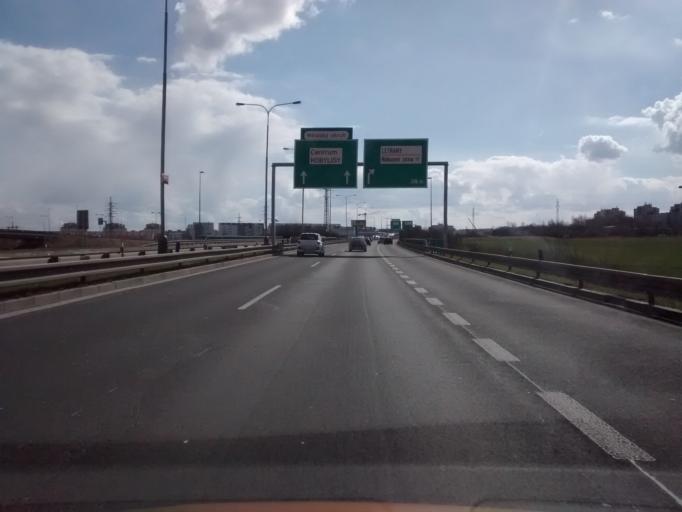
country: CZ
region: Praha
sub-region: Praha 9
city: Strizkov
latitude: 50.1387
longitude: 14.4940
